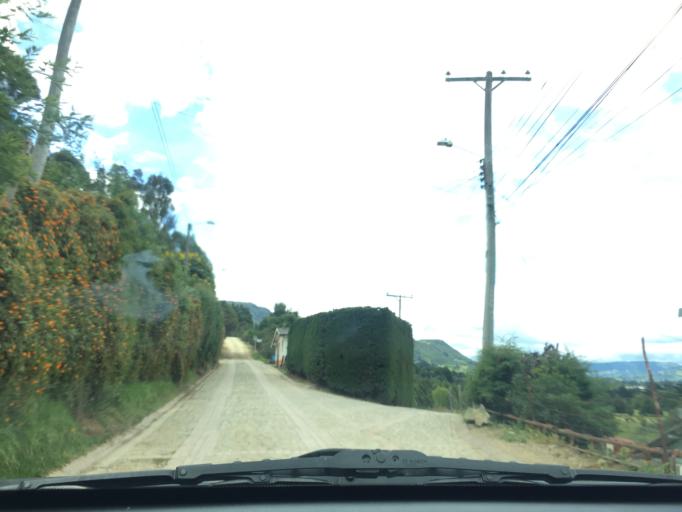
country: CO
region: Cundinamarca
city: Tabio
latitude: 4.9180
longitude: -74.1059
